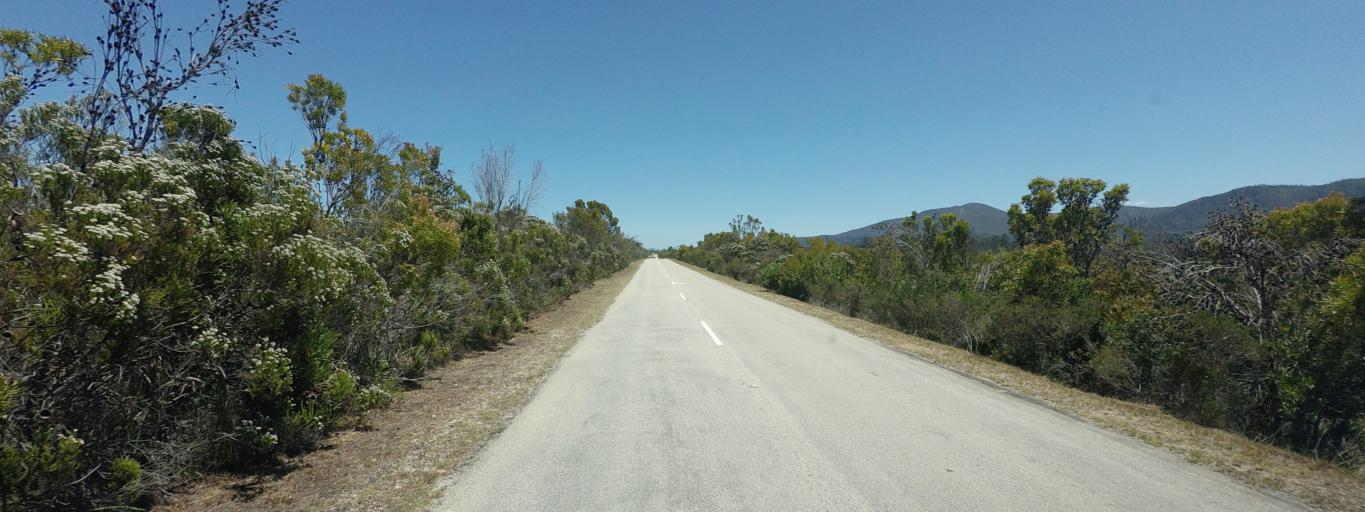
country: ZA
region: Western Cape
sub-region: Eden District Municipality
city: Plettenberg Bay
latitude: -33.9592
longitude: 23.5235
